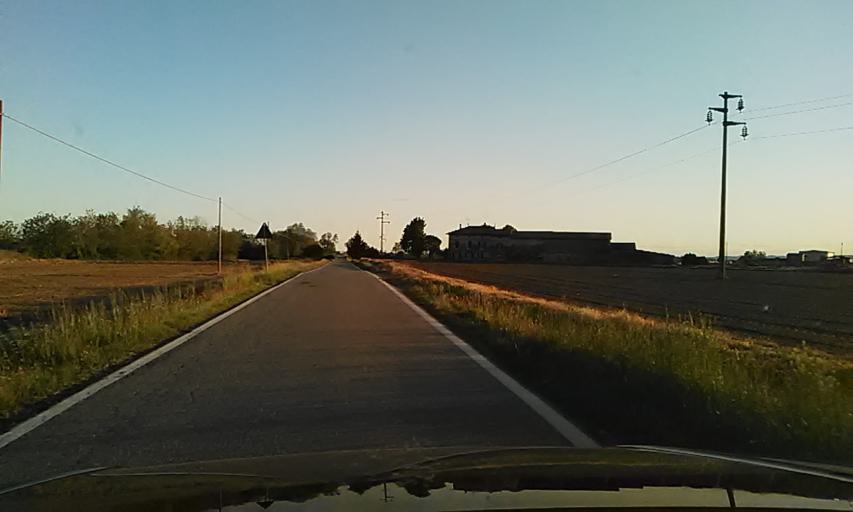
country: IT
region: Piedmont
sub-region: Provincia di Vercelli
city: Buronzo
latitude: 45.5040
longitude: 8.2907
